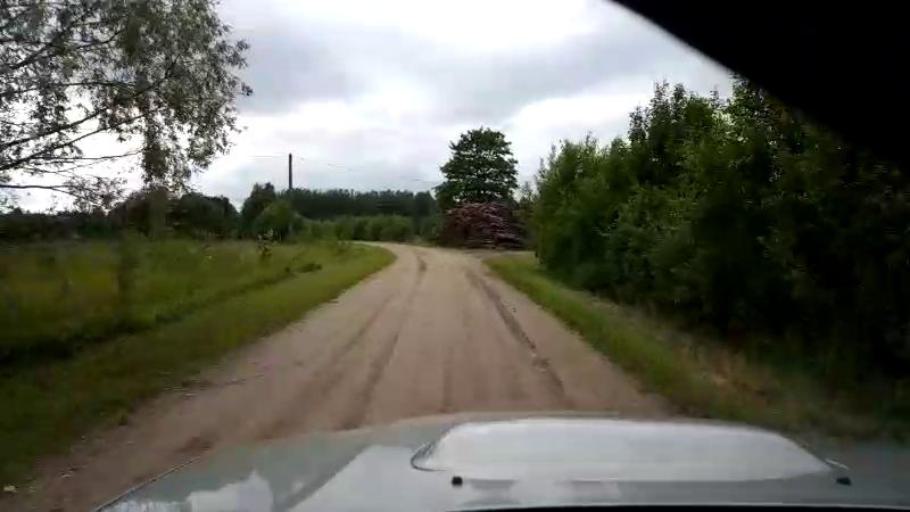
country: EE
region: Paernumaa
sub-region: Halinga vald
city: Parnu-Jaagupi
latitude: 58.5637
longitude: 24.5716
